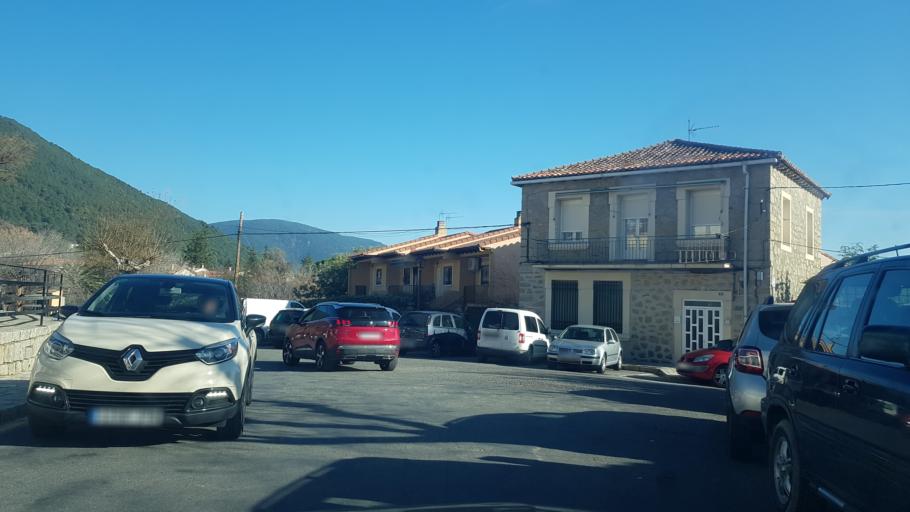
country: ES
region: Castille and Leon
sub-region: Provincia de Avila
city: Piedralaves
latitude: 40.3178
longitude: -4.6962
